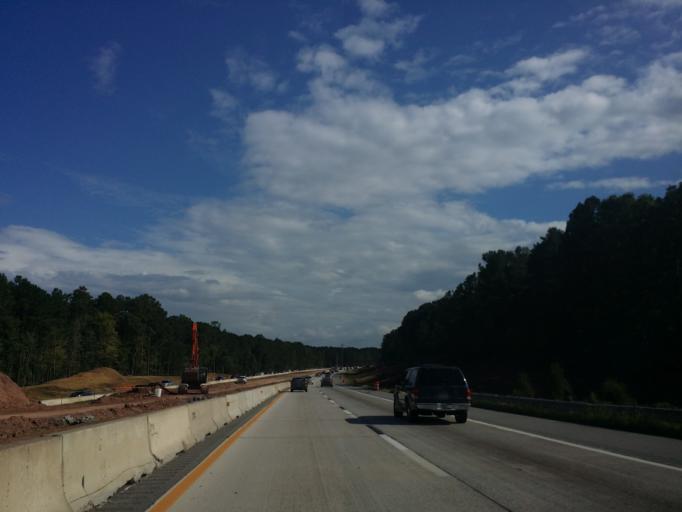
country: US
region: North Carolina
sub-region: Durham County
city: Durham
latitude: 35.9637
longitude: -78.8656
